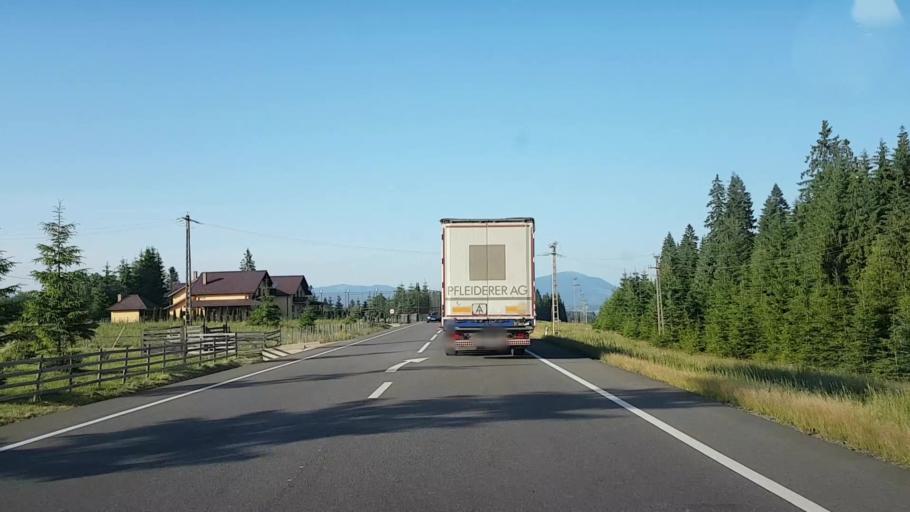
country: RO
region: Suceava
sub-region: Comuna Poiana Stampei
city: Poiana Stampei
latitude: 47.2940
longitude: 25.0820
